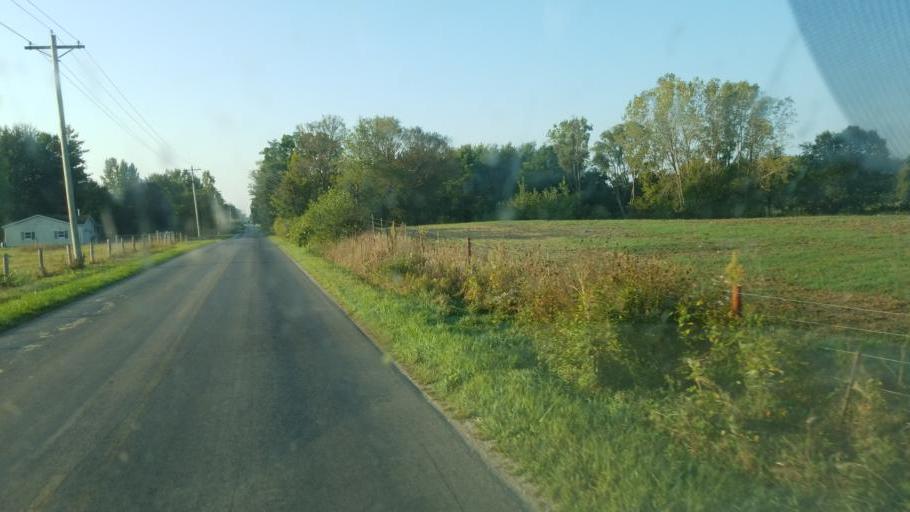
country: US
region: Indiana
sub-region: LaGrange County
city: Lagrange
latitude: 41.5947
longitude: -85.4242
